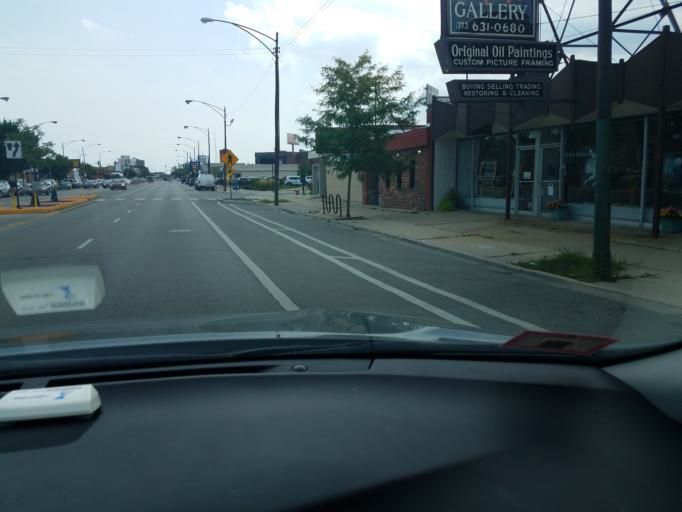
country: US
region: Illinois
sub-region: Cook County
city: Harwood Heights
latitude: 41.9780
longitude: -87.7699
